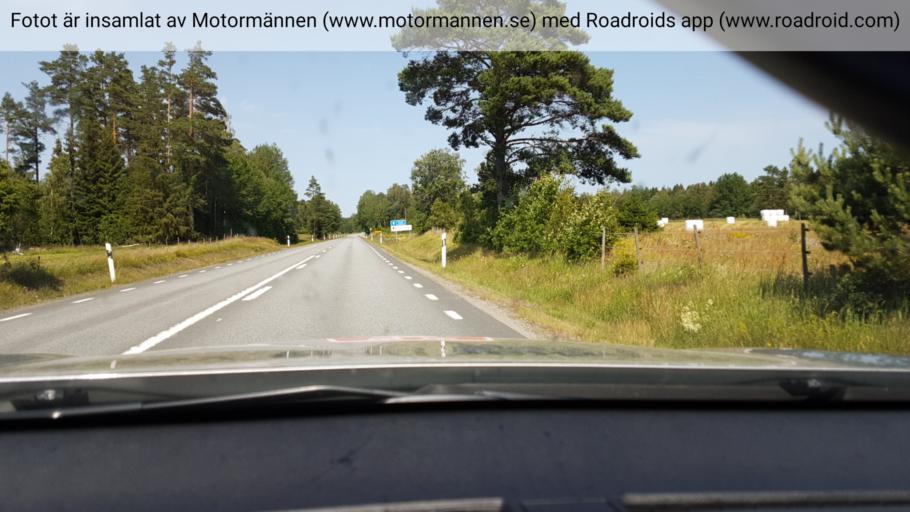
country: SE
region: Joenkoeping
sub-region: Nassjo Kommun
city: Bodafors
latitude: 57.4841
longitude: 14.7877
